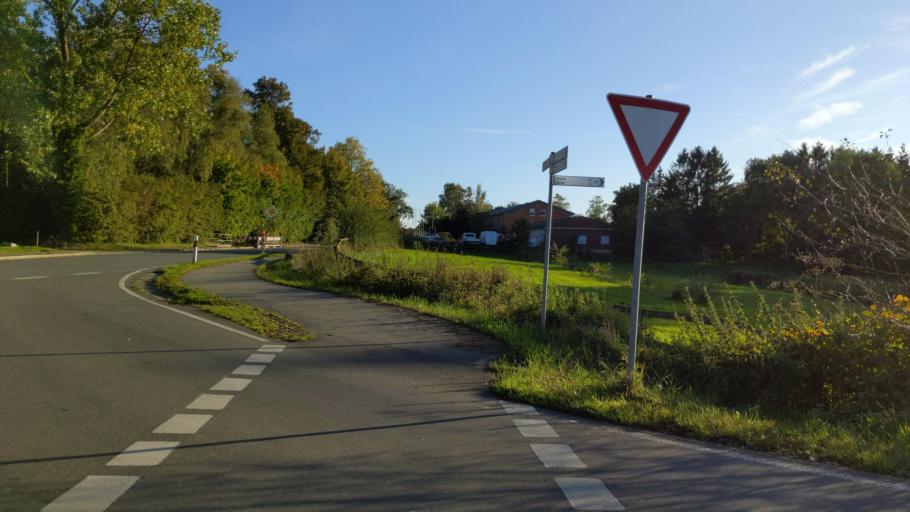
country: DE
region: Schleswig-Holstein
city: Ahrensbok
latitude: 54.0262
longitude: 10.5641
